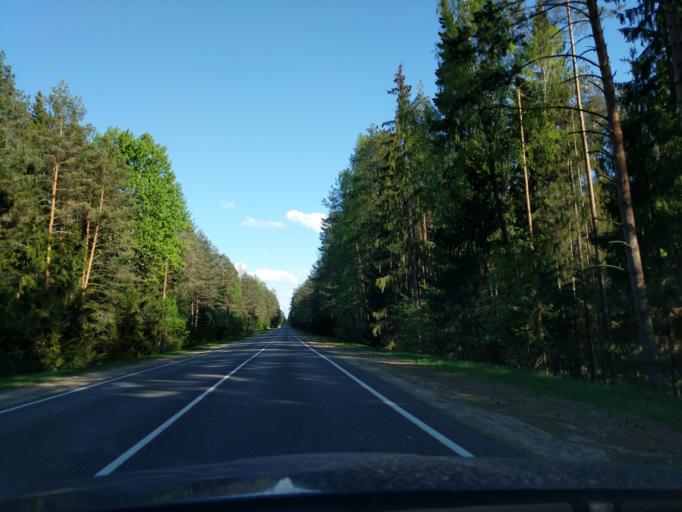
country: BY
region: Minsk
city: Myadzyel
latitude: 54.8072
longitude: 26.9882
